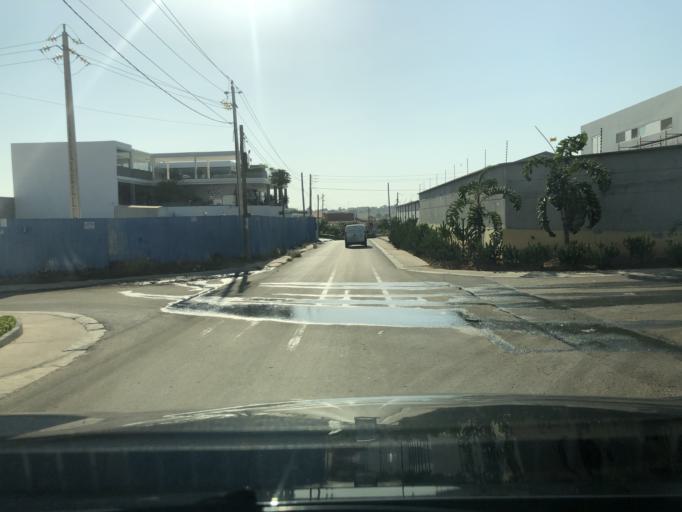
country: AO
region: Luanda
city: Luanda
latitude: -8.9071
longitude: 13.2230
